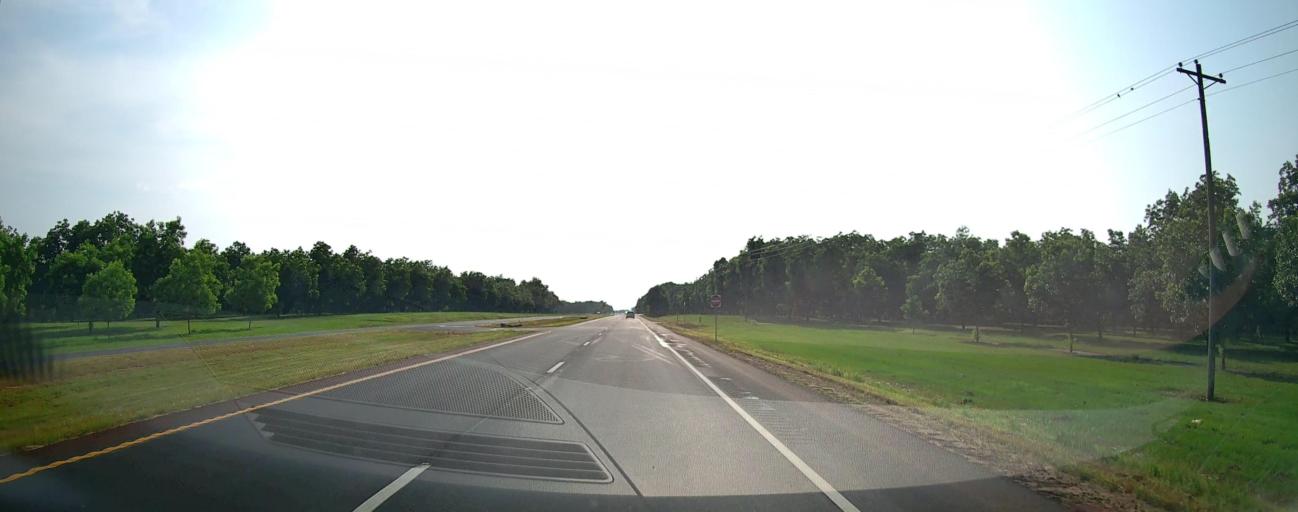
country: US
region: Georgia
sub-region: Peach County
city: Fort Valley
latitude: 32.5779
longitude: -83.8871
